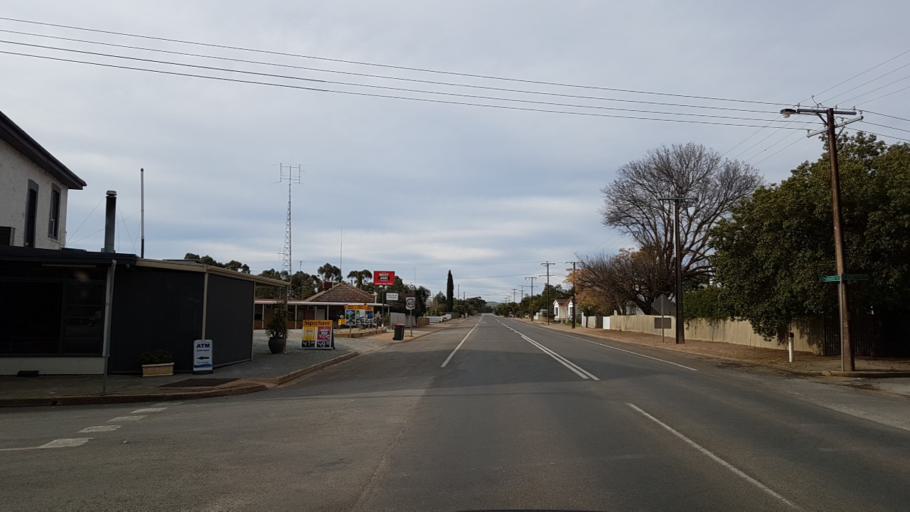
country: AU
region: South Australia
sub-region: Northern Areas
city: Jamestown
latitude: -33.2000
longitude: 138.6066
